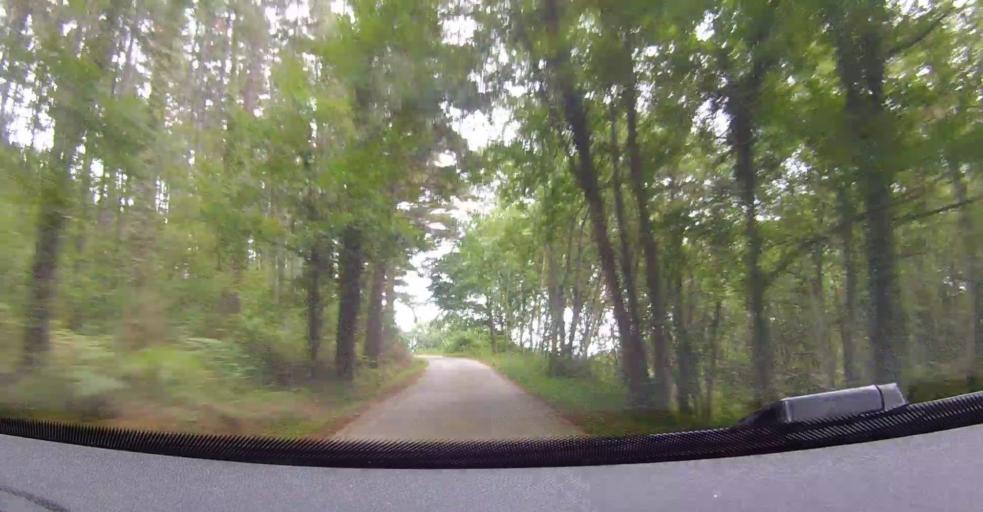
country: ES
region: Basque Country
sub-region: Bizkaia
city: Urrestieta
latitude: 43.2287
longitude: -3.1693
